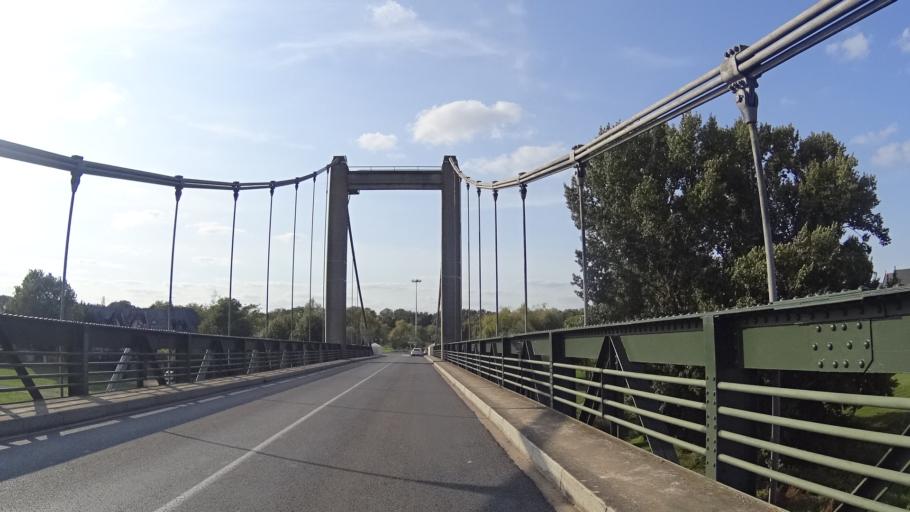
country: FR
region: Pays de la Loire
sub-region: Departement de Maine-et-Loire
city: Bouchemaine
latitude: 47.4202
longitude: -0.6082
